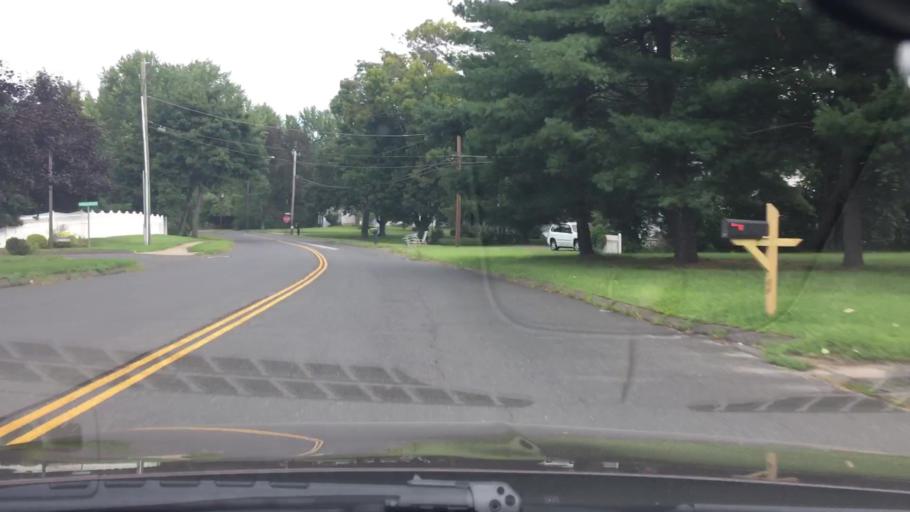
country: US
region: Connecticut
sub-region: Tolland County
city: Rockville
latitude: 41.8293
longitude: -72.4900
